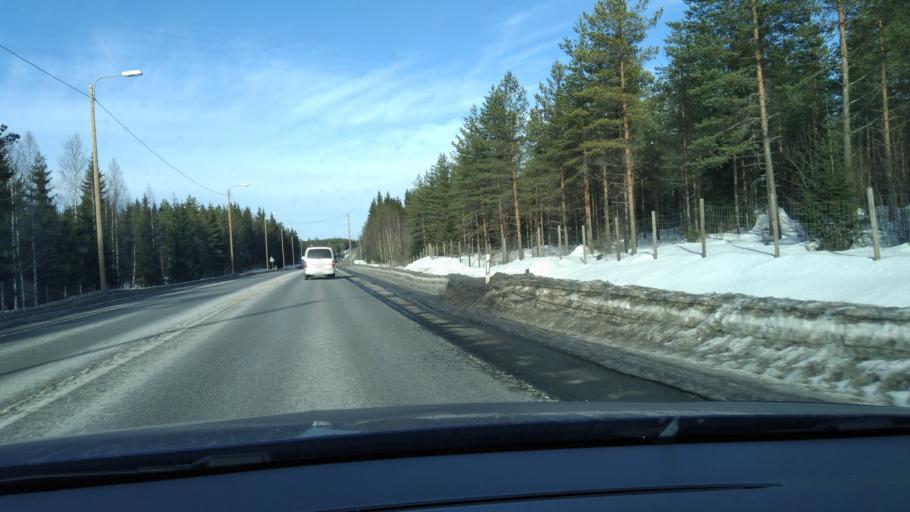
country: FI
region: Pirkanmaa
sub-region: Tampere
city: Orivesi
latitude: 61.6572
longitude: 24.2516
